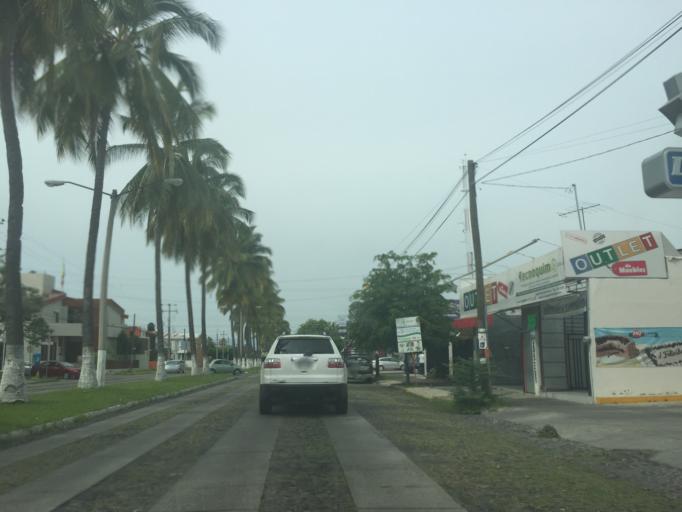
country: MX
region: Colima
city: Colima
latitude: 19.2559
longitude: -103.7173
